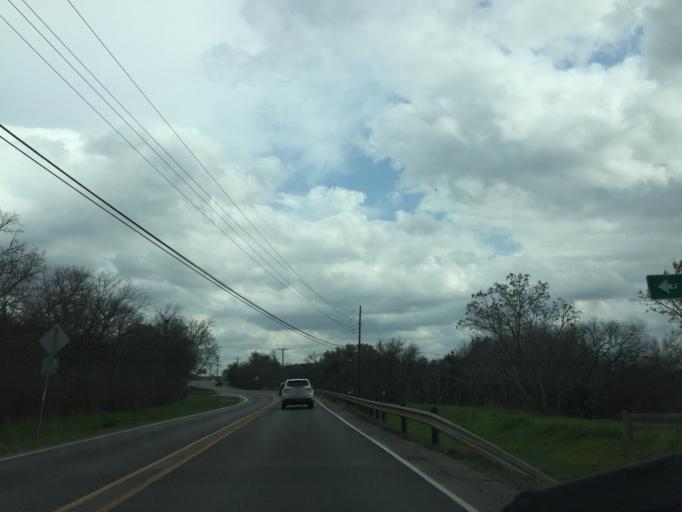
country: US
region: Texas
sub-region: Travis County
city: Manchaca
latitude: 30.1420
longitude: -97.8414
